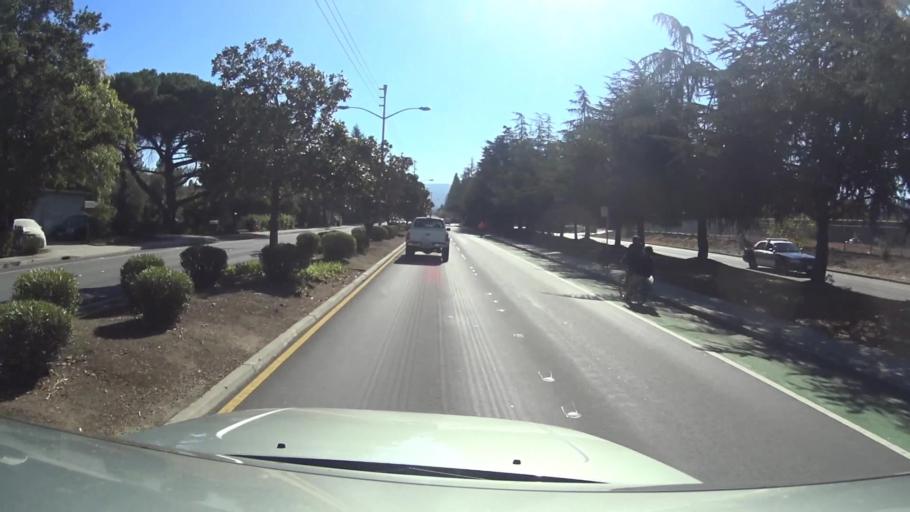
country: US
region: California
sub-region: Santa Clara County
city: Cupertino
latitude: 37.3174
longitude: -122.0416
